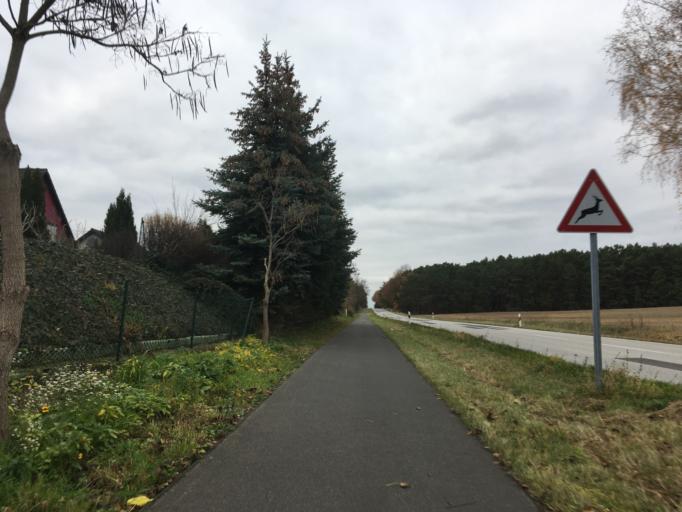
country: DE
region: Brandenburg
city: Mixdorf
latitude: 52.1921
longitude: 14.4632
